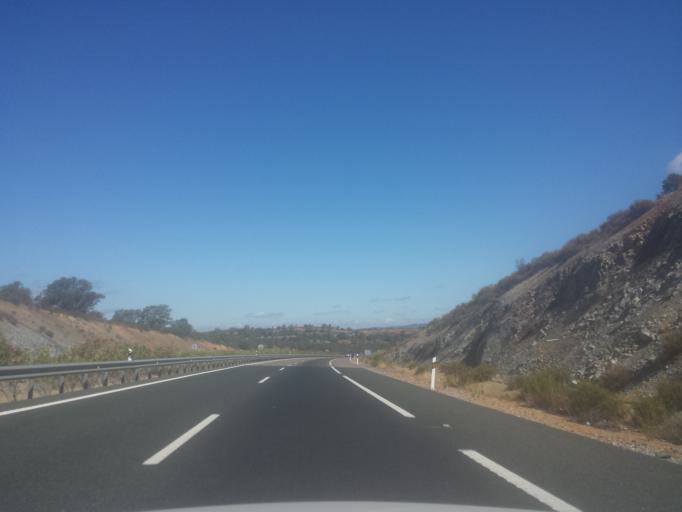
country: ES
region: Andalusia
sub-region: Provincia de Sevilla
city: El Ronquillo
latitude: 37.7950
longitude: -6.1987
